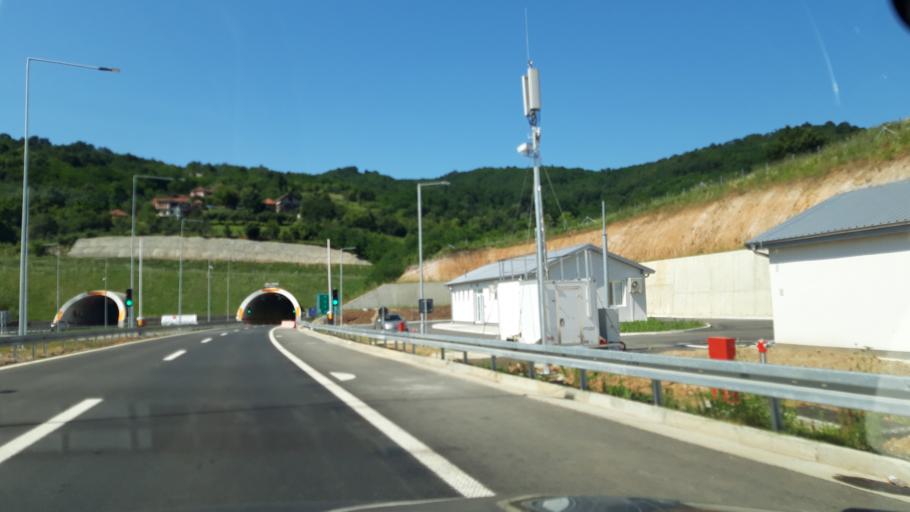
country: RS
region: Central Serbia
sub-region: Pcinjski Okrug
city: Vladicin Han
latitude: 42.7295
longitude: 22.0735
